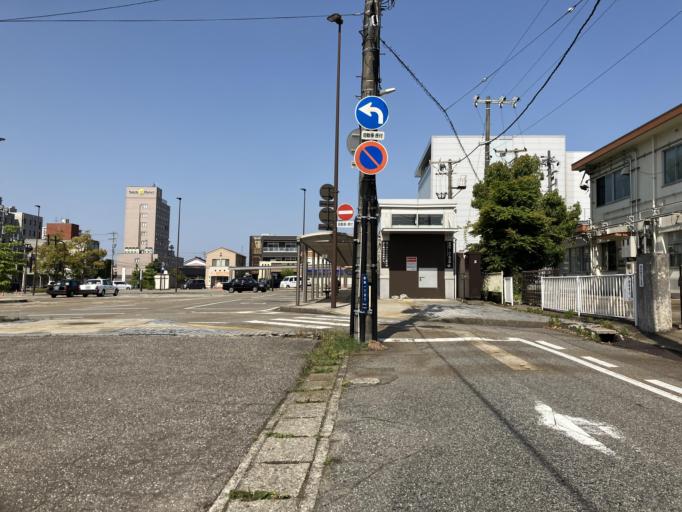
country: JP
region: Toyama
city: Takaoka
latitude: 36.7405
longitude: 137.0163
